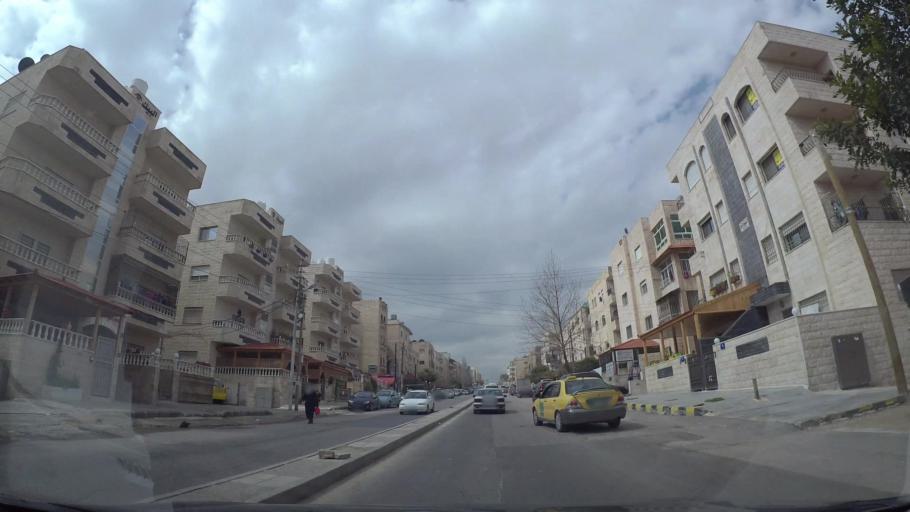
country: JO
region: Amman
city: Amman
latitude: 31.9874
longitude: 35.9273
